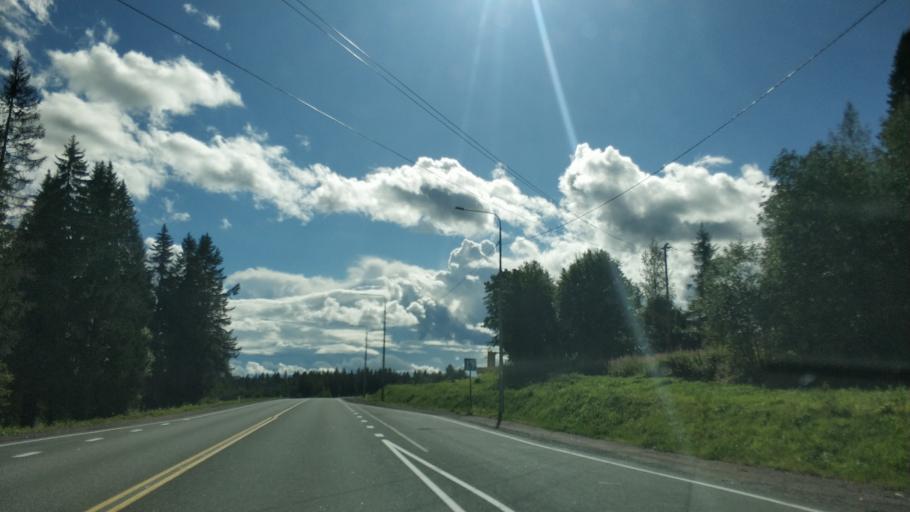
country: RU
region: Republic of Karelia
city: Ruskeala
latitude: 61.8841
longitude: 30.6438
